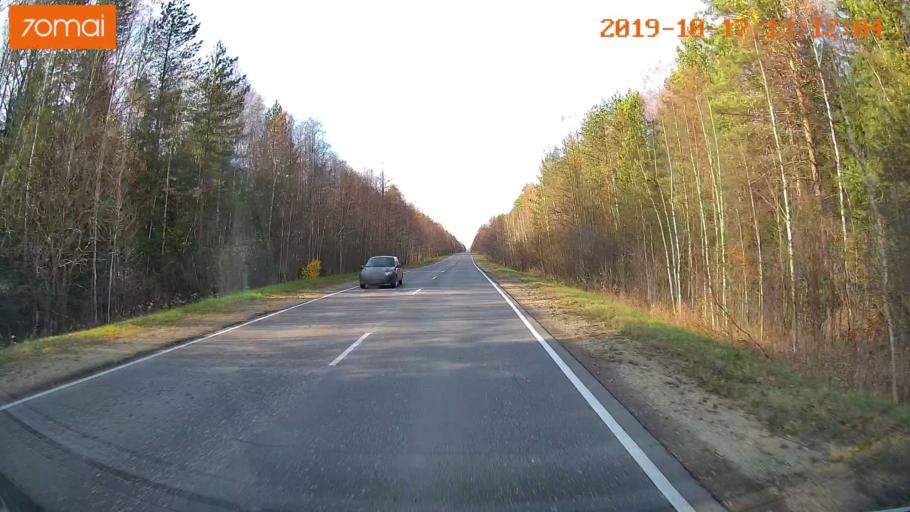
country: RU
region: Rjazan
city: Gus'-Zheleznyy
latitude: 55.0331
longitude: 41.2213
